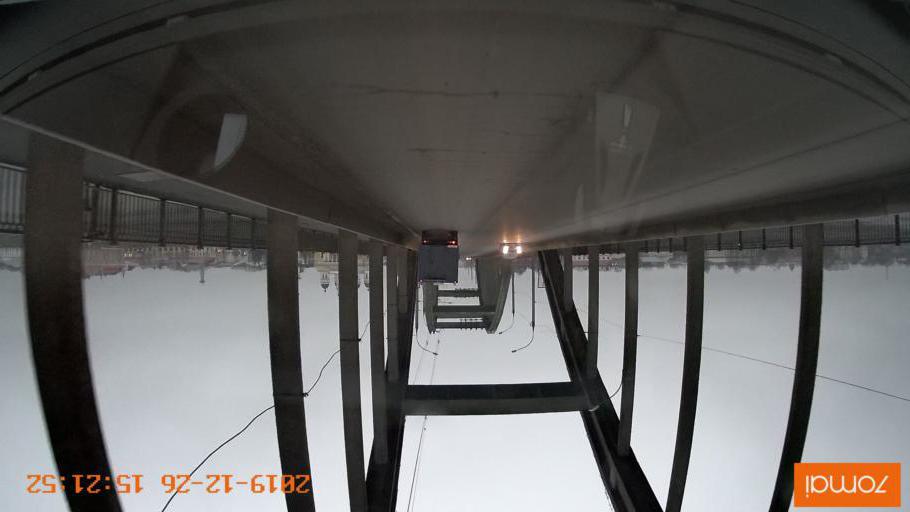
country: RU
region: Jaroslavl
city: Rybinsk
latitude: 58.0509
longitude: 38.8620
